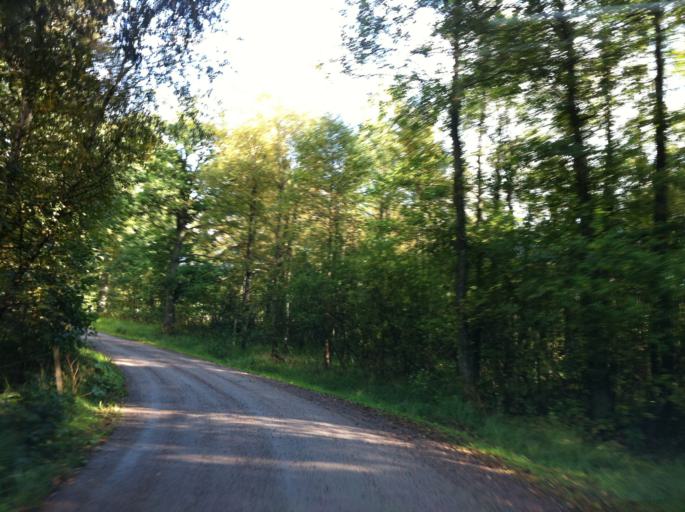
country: SE
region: Skane
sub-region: Hassleholms Kommun
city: Sosdala
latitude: 56.1259
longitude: 13.5932
